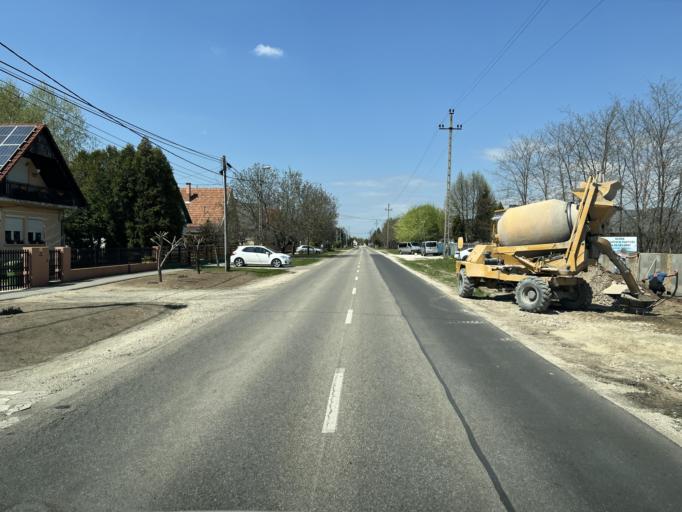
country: HU
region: Pest
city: Inarcs
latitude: 47.2518
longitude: 19.3338
